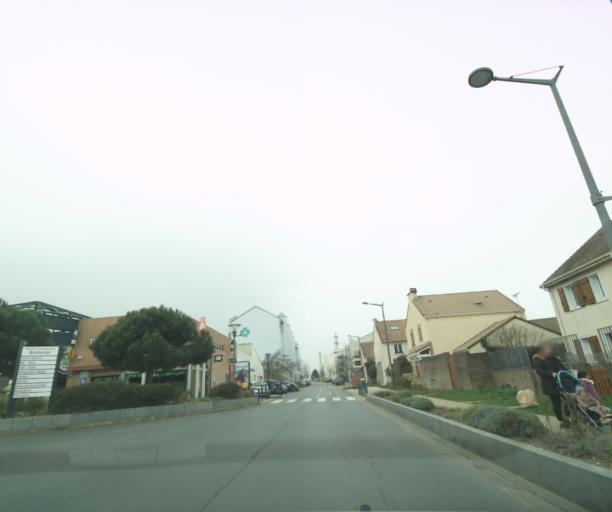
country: FR
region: Ile-de-France
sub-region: Departement du Val-d'Oise
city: Courdimanche
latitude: 49.0530
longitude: 2.0180
